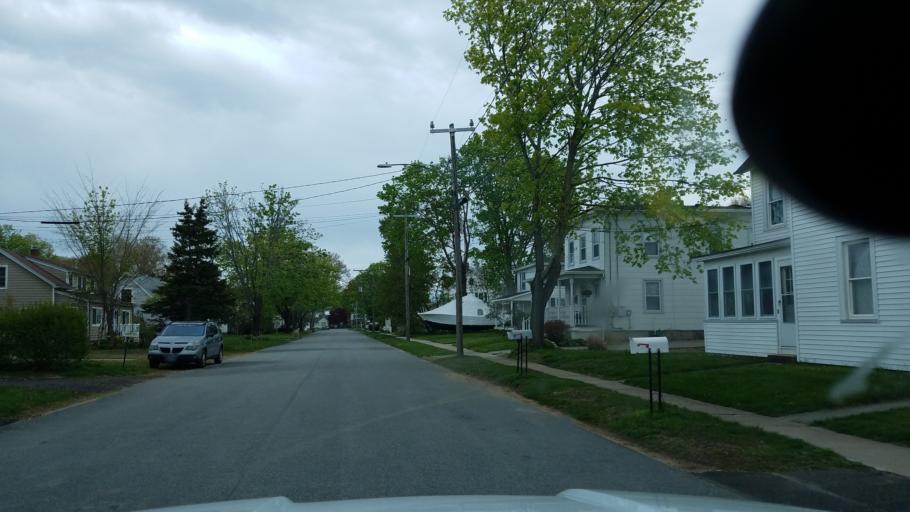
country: US
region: Connecticut
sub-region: New London County
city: Niantic
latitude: 41.3275
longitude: -72.1899
